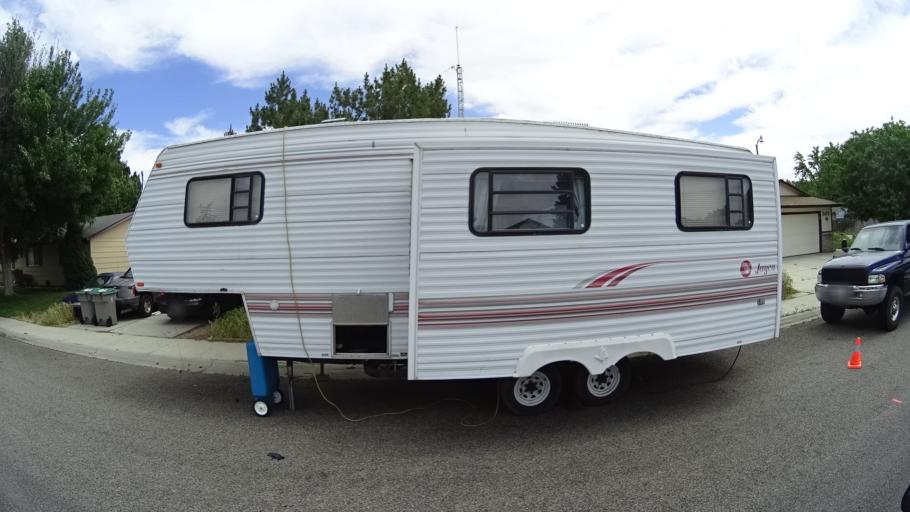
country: US
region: Idaho
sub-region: Ada County
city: Eagle
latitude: 43.6368
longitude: -116.3244
